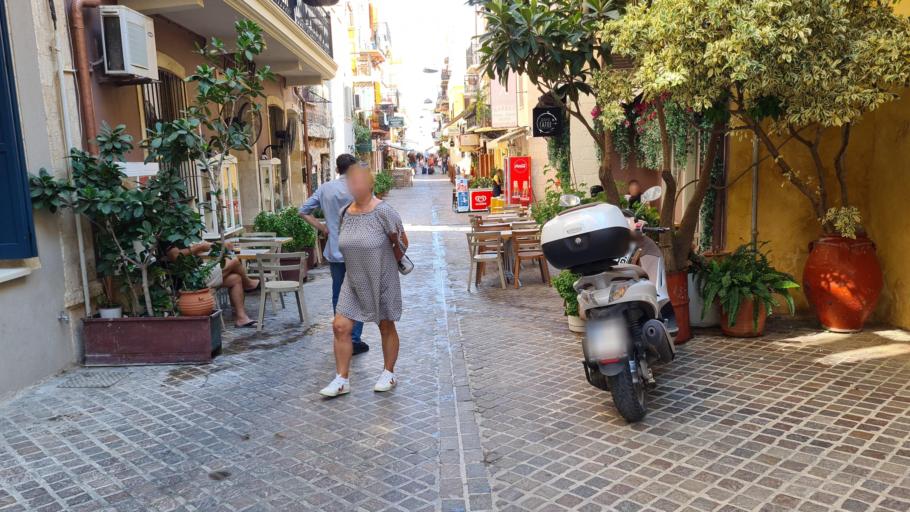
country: GR
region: Crete
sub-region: Nomos Chanias
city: Chania
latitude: 35.5169
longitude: 24.0155
